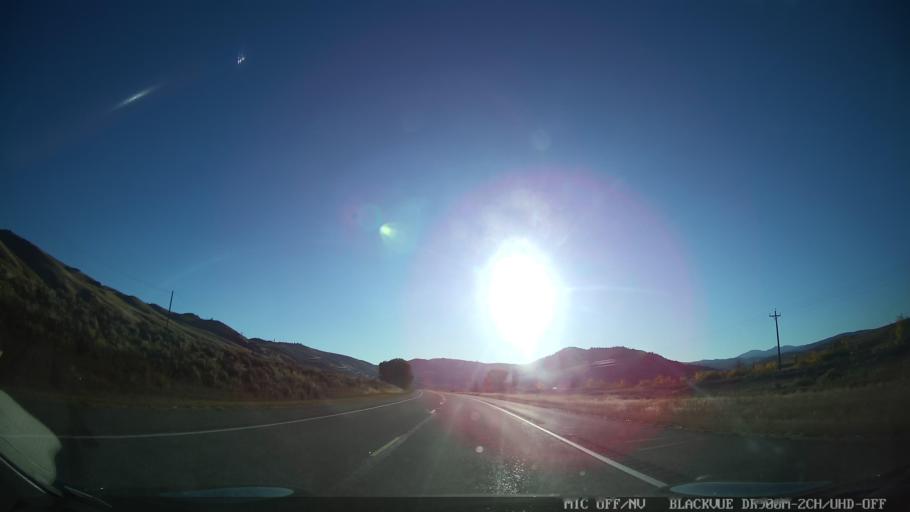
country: US
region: Colorado
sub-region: Grand County
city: Hot Sulphur Springs
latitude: 40.0518
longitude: -106.1573
